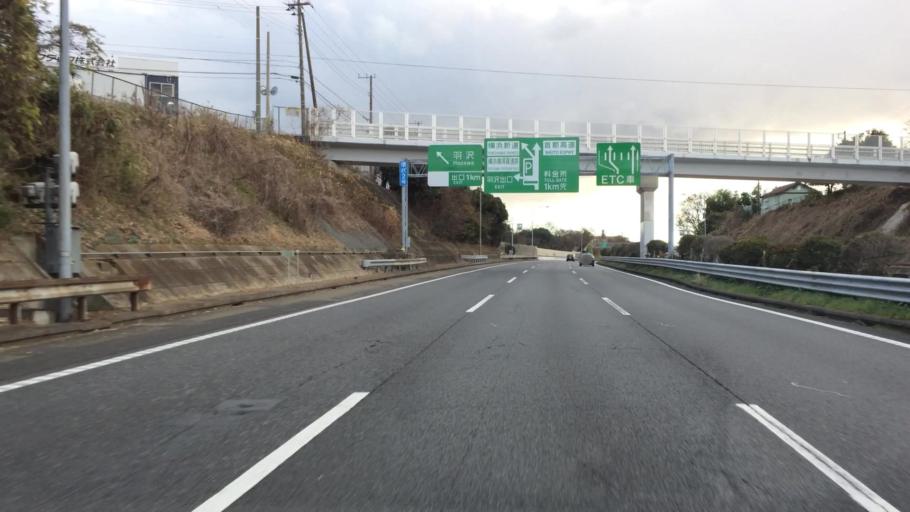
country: JP
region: Kanagawa
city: Yokohama
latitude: 35.4949
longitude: 139.5919
